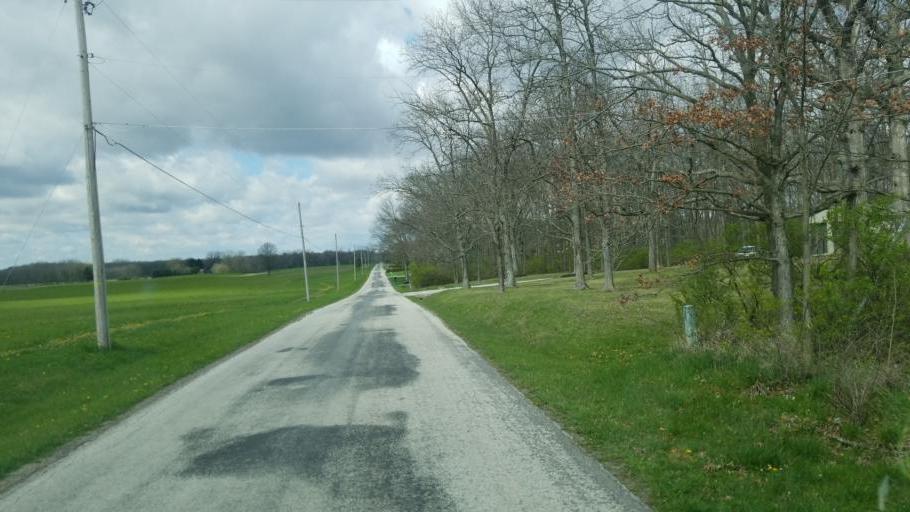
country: US
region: Ohio
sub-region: Delaware County
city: Delaware
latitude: 40.3296
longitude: -83.1398
